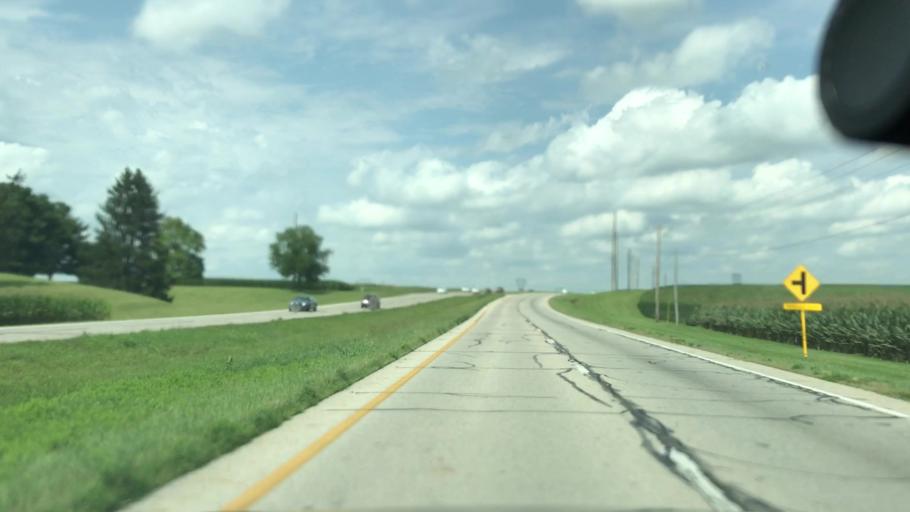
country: US
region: Ohio
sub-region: Pickaway County
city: Logan Elm Village
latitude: 39.5362
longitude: -82.9669
